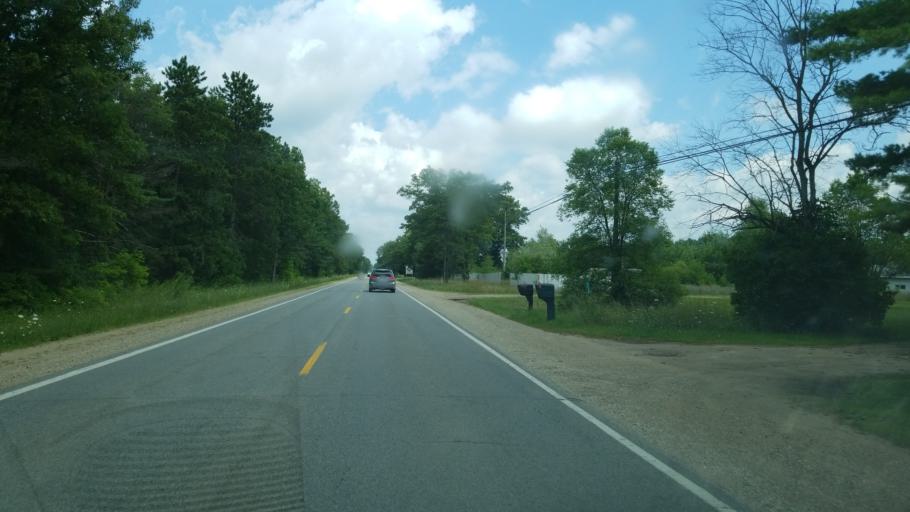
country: US
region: Michigan
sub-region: Montcalm County
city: Howard City
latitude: 43.4140
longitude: -85.4651
